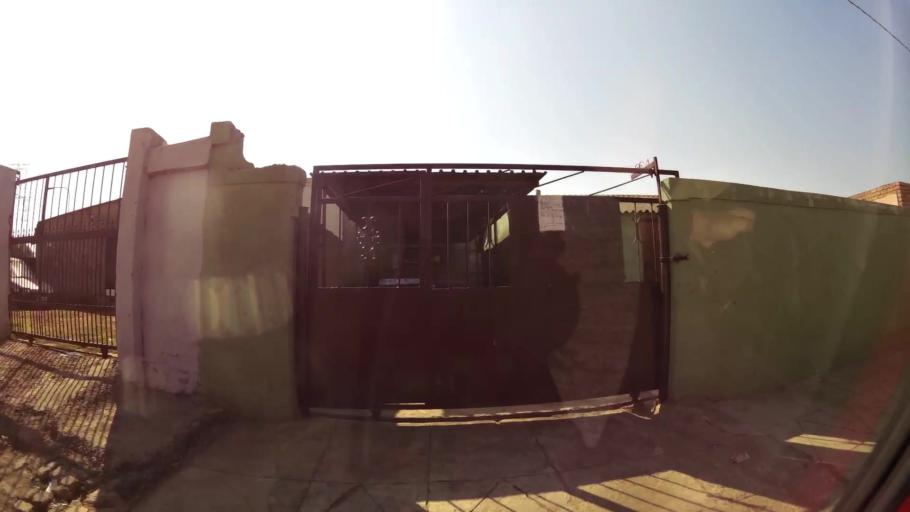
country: ZA
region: Gauteng
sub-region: City of Johannesburg Metropolitan Municipality
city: Soweto
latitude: -26.2471
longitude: 27.9355
